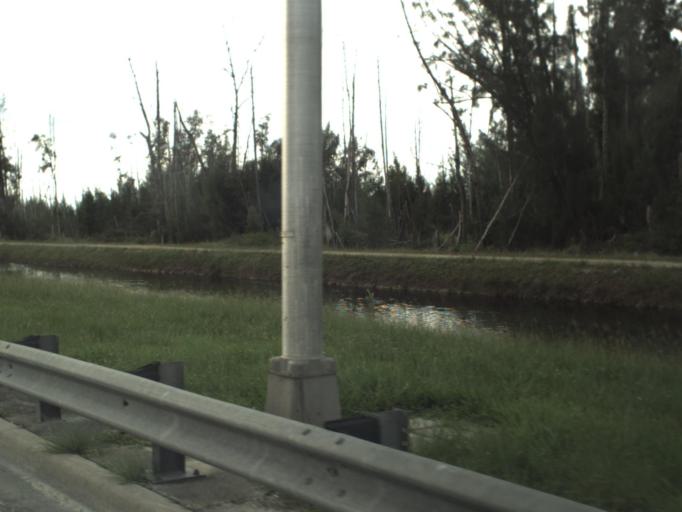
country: US
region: Florida
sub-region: Miami-Dade County
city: Tamiami
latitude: 25.7611
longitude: -80.4234
